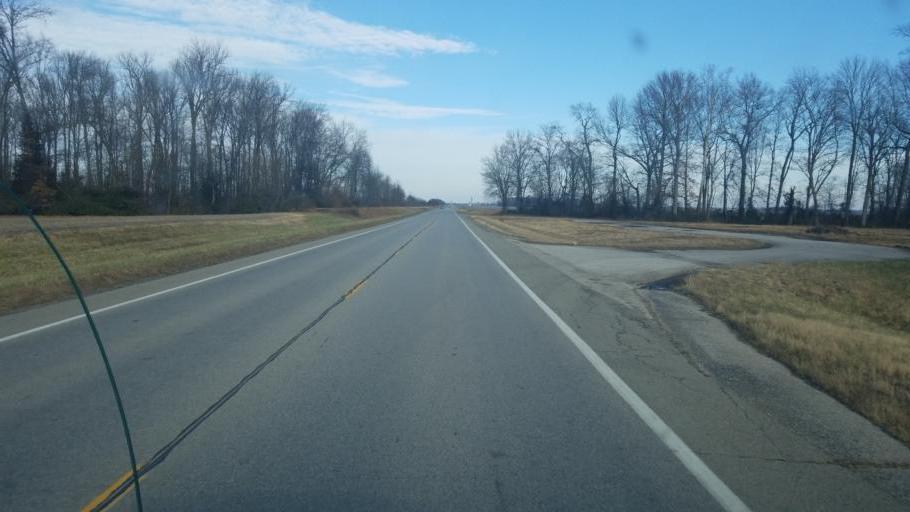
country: US
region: Illinois
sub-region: White County
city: Carmi
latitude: 38.1216
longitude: -88.1097
